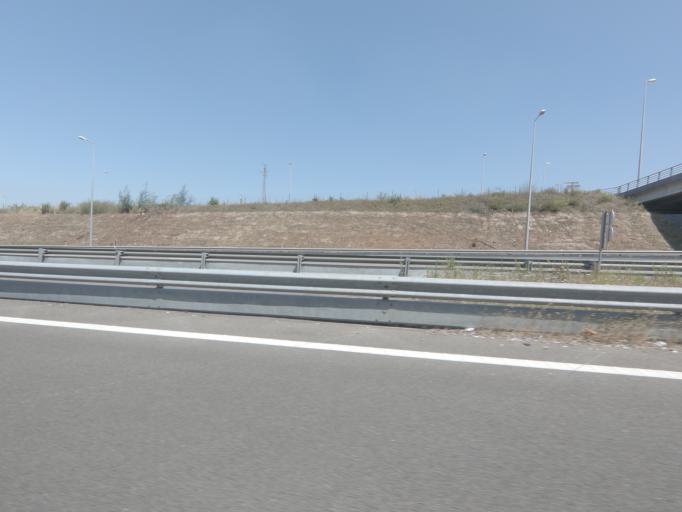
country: PT
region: Porto
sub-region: Matosinhos
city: Sao Mamede de Infesta
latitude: 41.2006
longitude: -8.6094
